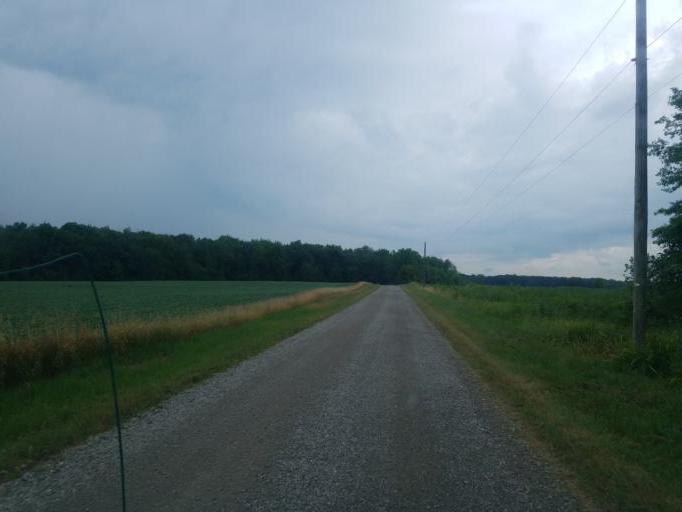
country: US
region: Ohio
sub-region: Defiance County
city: Hicksville
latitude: 41.3623
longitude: -84.8040
